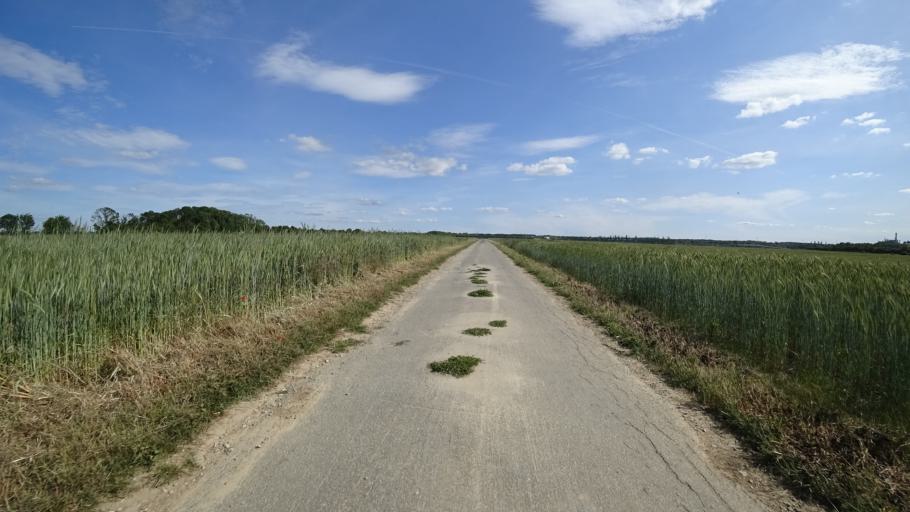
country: DE
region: North Rhine-Westphalia
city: Erwitte
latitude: 51.6105
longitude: 8.3669
